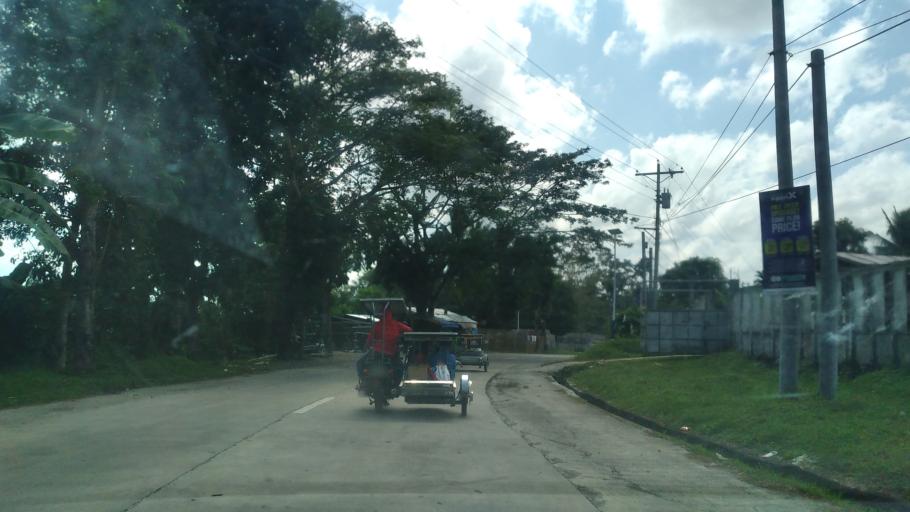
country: PH
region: Calabarzon
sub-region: Province of Quezon
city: Macalelon
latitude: 13.7575
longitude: 122.1431
